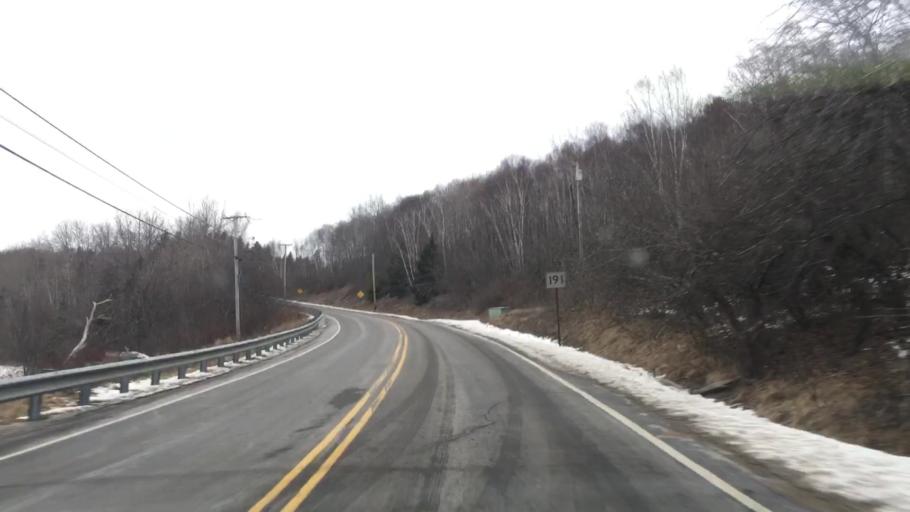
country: US
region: Maine
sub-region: Washington County
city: Machiasport
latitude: 44.7136
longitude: -67.3750
